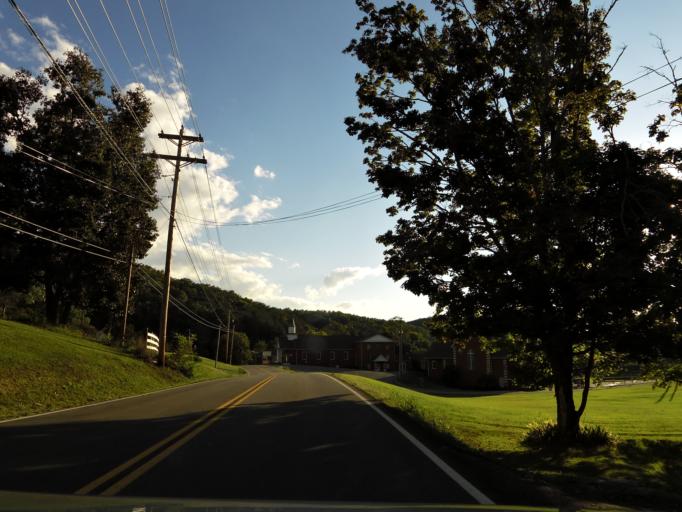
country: US
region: Tennessee
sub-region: Grainger County
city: Rutledge
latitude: 36.2616
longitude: -83.5249
